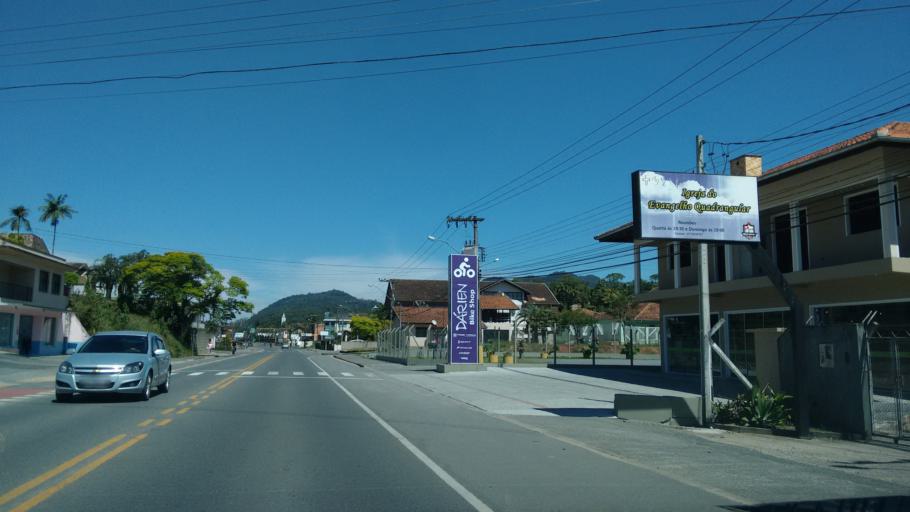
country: BR
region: Santa Catarina
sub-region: Pomerode
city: Pomerode
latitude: -26.7478
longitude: -49.1738
